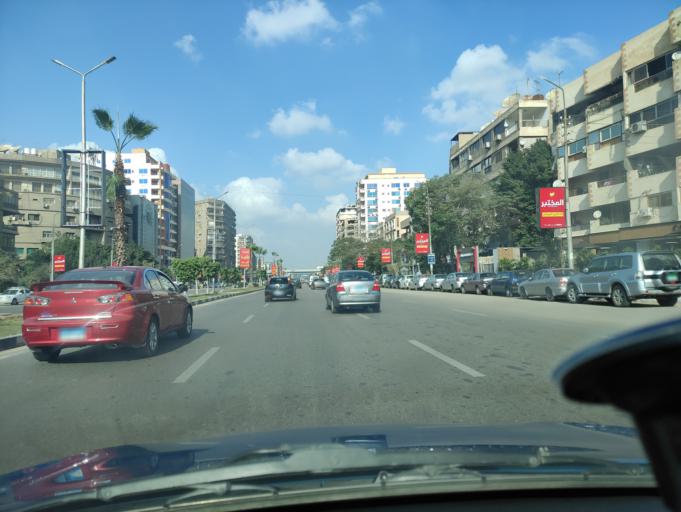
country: EG
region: Muhafazat al Qahirah
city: Cairo
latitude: 30.0875
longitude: 31.3412
